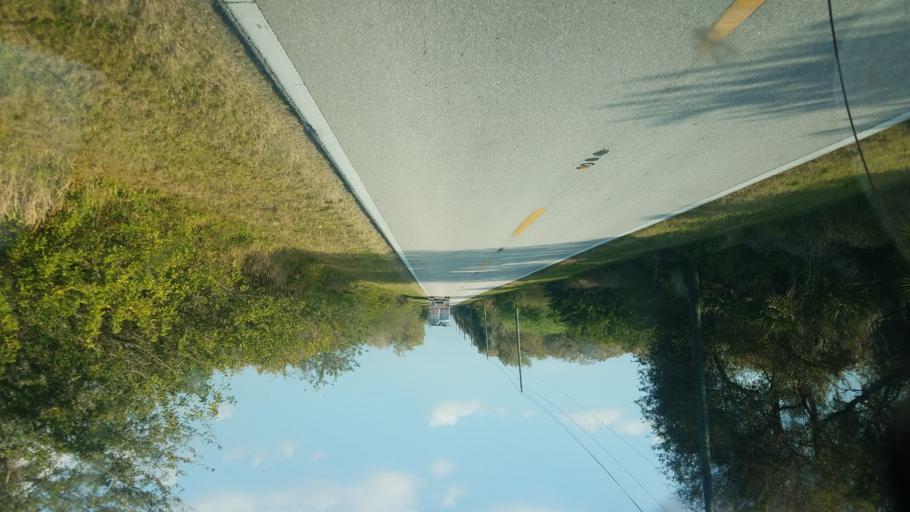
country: US
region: Florida
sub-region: Hardee County
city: Bowling Green
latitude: 27.6928
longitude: -81.9567
